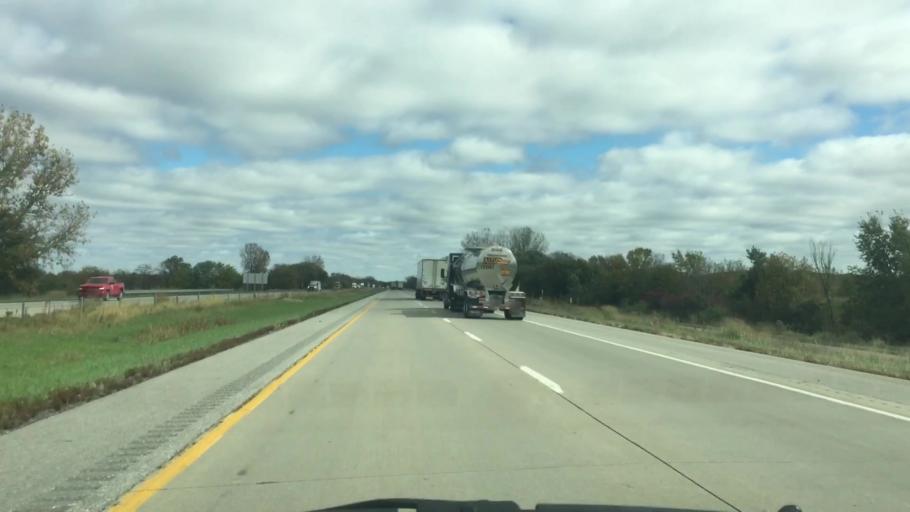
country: US
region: Iowa
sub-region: Jasper County
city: Colfax
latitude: 41.6943
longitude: -93.2359
